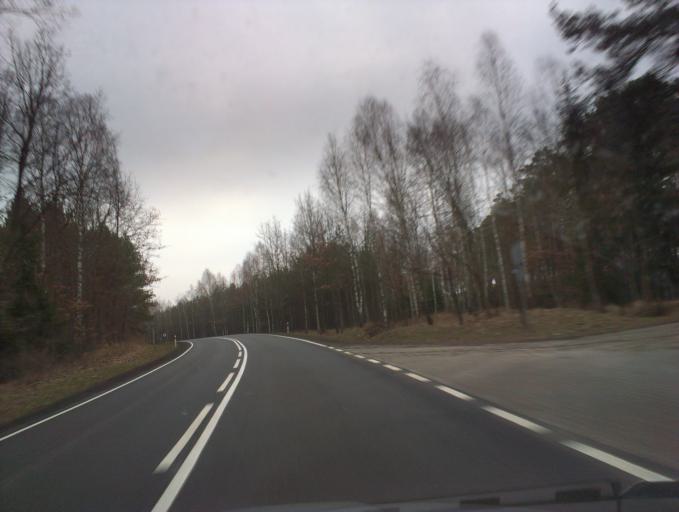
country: PL
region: Greater Poland Voivodeship
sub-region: Powiat pilski
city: Pila
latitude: 53.2375
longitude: 16.7927
